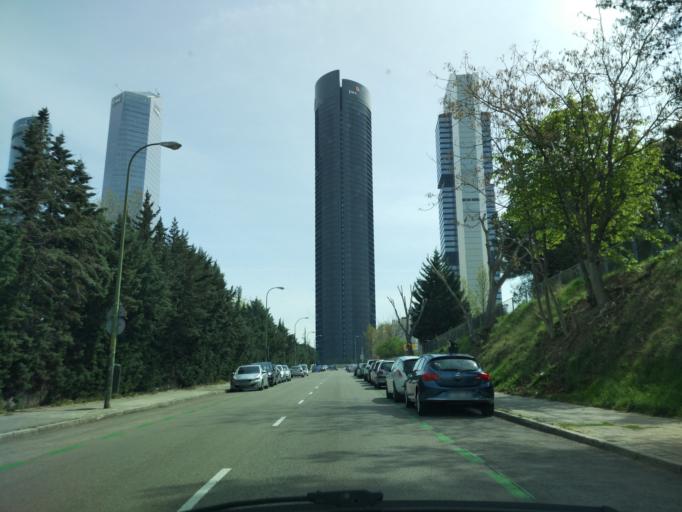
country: ES
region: Madrid
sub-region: Provincia de Madrid
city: Chamartin
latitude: 40.4774
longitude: -3.6936
